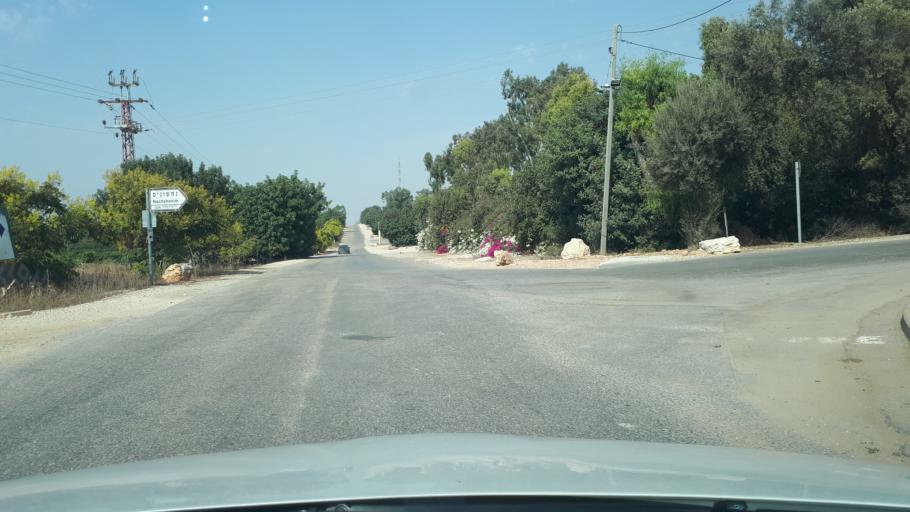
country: IL
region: Central District
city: Rosh Ha'Ayin
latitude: 32.0622
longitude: 34.9459
